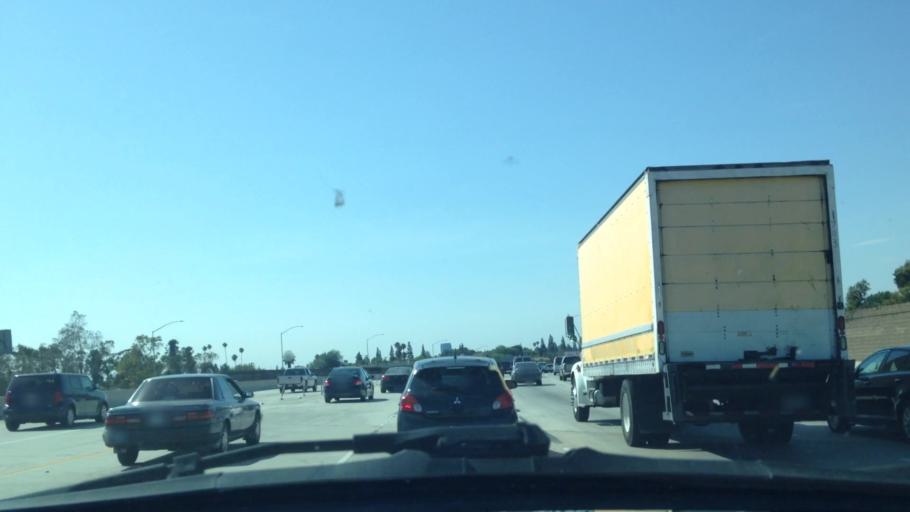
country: US
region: California
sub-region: Orange County
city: Santa Ana
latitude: 33.7606
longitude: -117.8663
